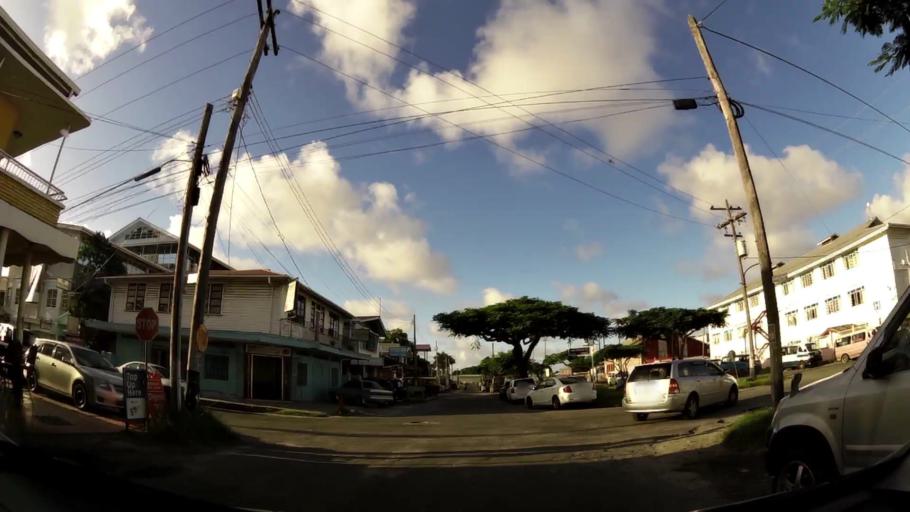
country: GY
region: Demerara-Mahaica
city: Georgetown
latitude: 6.8165
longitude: -58.1573
